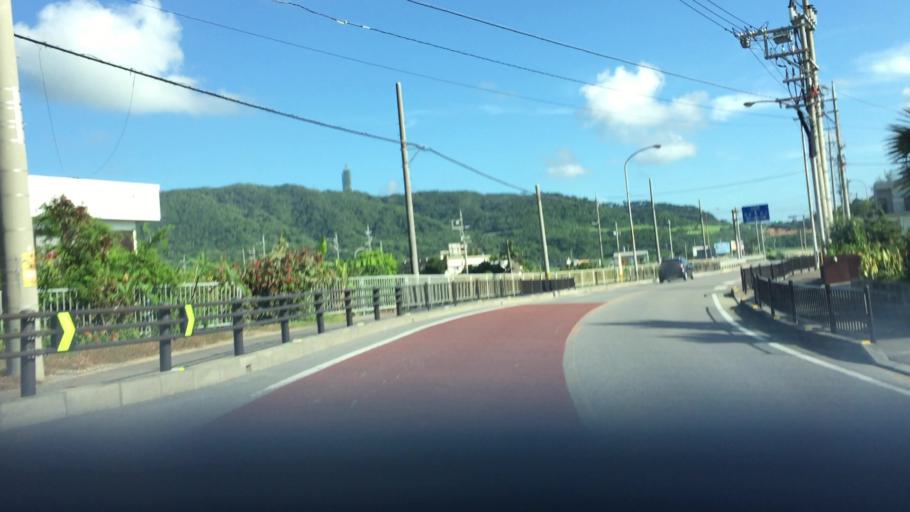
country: JP
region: Okinawa
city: Ishigaki
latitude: 24.3963
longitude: 124.1563
